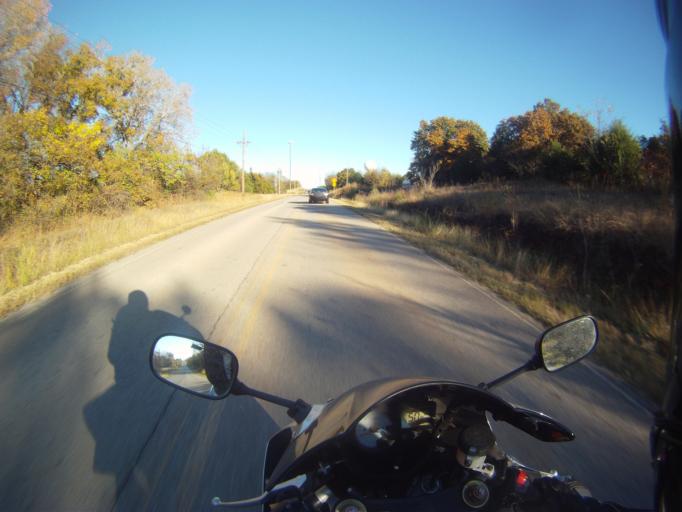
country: US
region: Oklahoma
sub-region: Payne County
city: Stillwater
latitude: 36.1303
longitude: -97.1006
